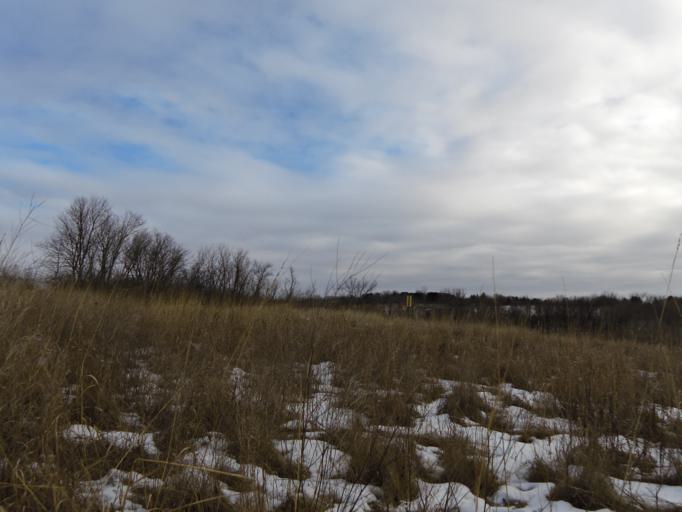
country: US
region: Wisconsin
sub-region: Pierce County
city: Prescott
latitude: 44.8010
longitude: -92.8270
